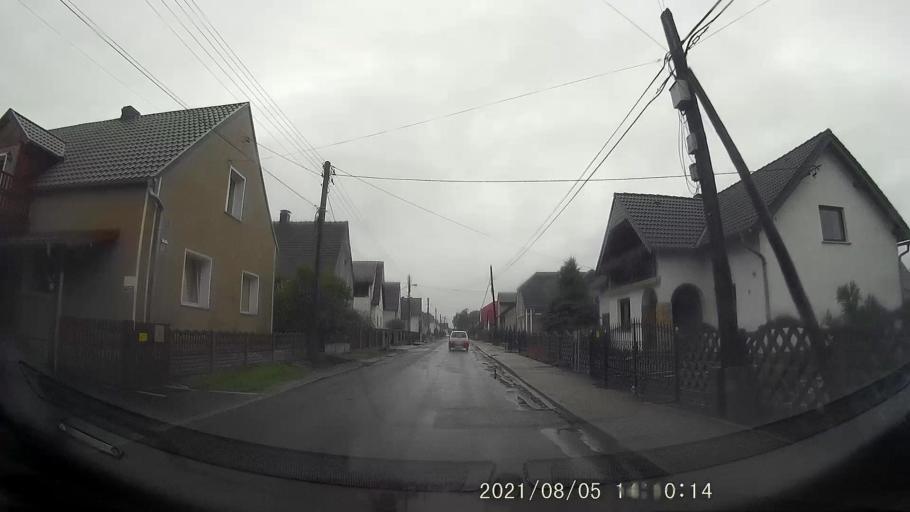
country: PL
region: Opole Voivodeship
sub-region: Powiat krapkowicki
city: Strzeleczki
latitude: 50.4707
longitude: 17.7914
